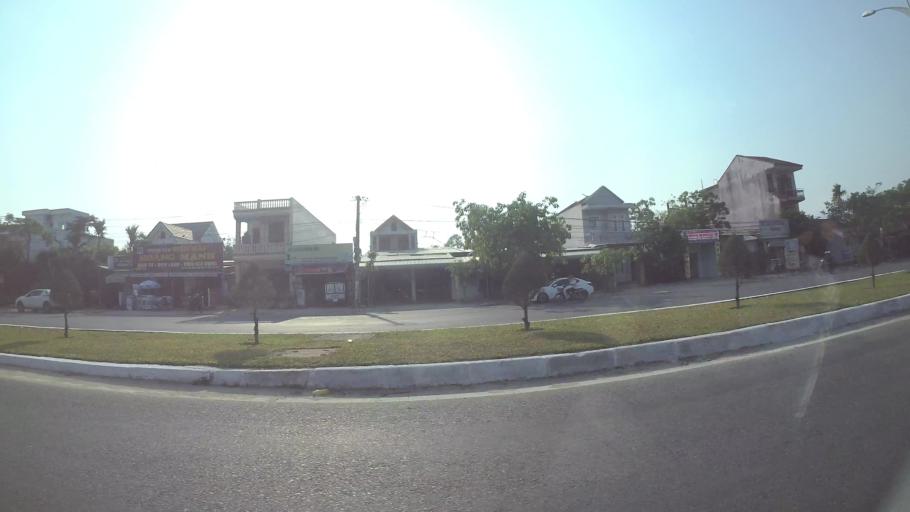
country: VN
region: Da Nang
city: Ngu Hanh Son
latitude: 15.9569
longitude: 108.2545
